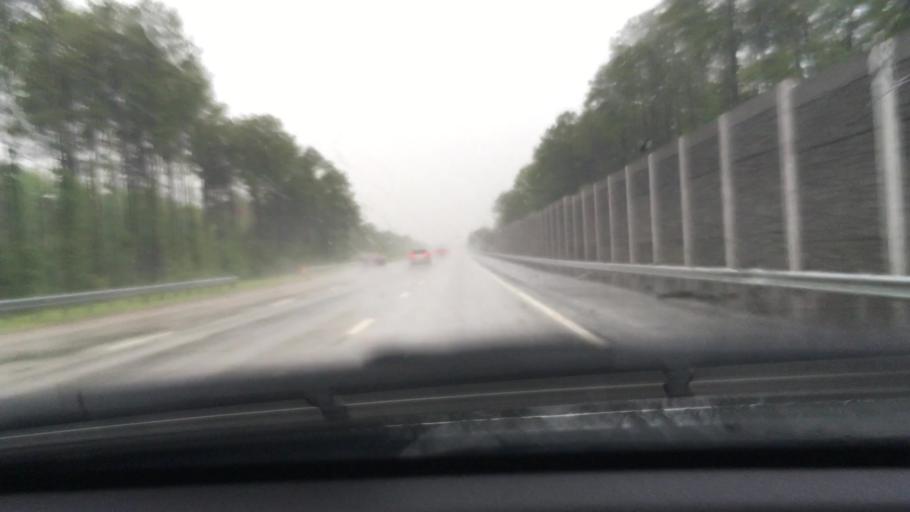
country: US
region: South Carolina
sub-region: Richland County
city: Woodfield
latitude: 34.0894
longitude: -80.8697
